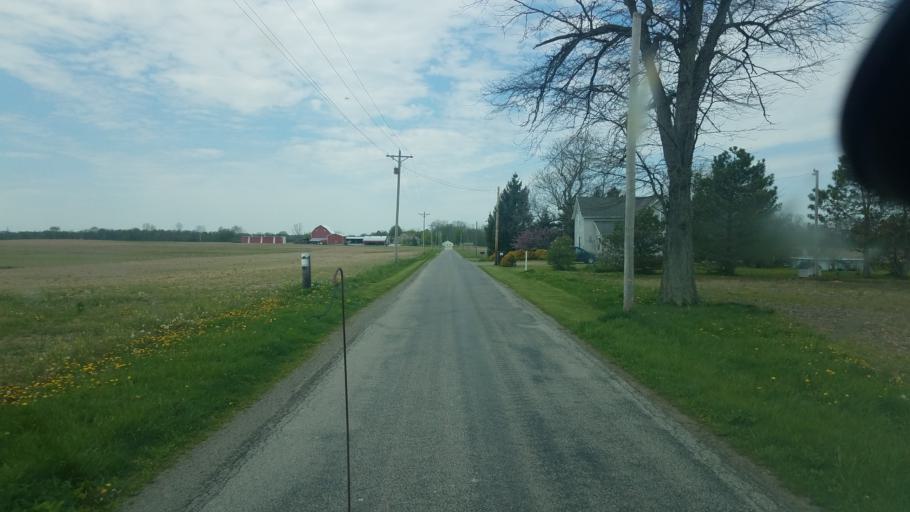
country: US
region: Ohio
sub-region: Hardin County
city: Ada
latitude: 40.7910
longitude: -83.8733
